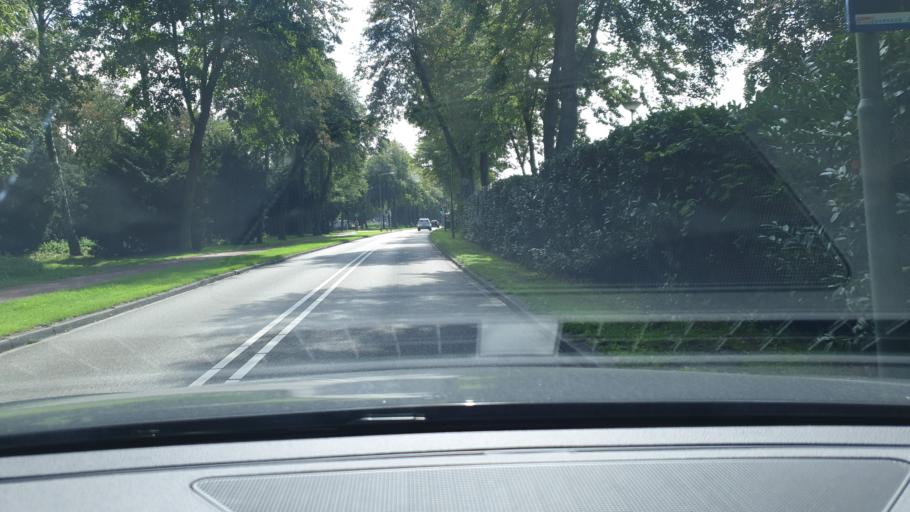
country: NL
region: Limburg
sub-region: Gemeente Venray
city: Venray
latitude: 51.5261
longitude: 5.9843
